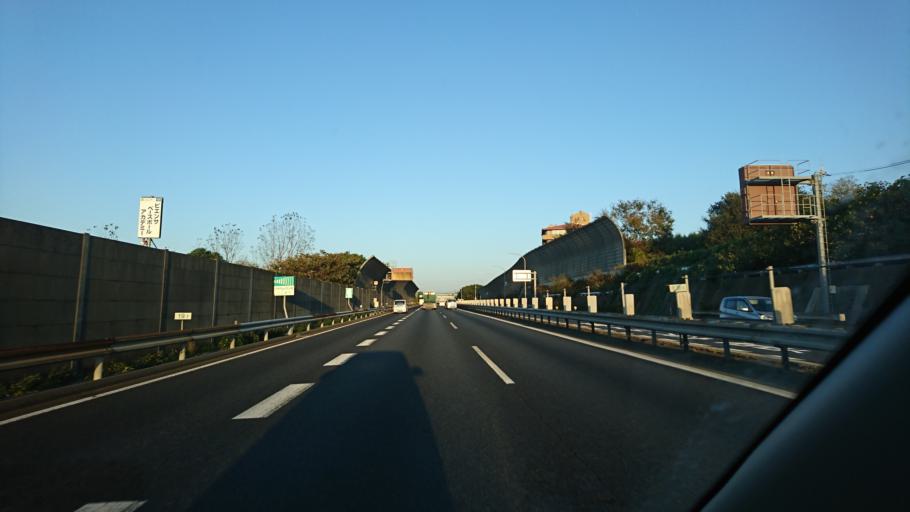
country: JP
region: Hyogo
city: Akashi
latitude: 34.7075
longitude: 134.9490
